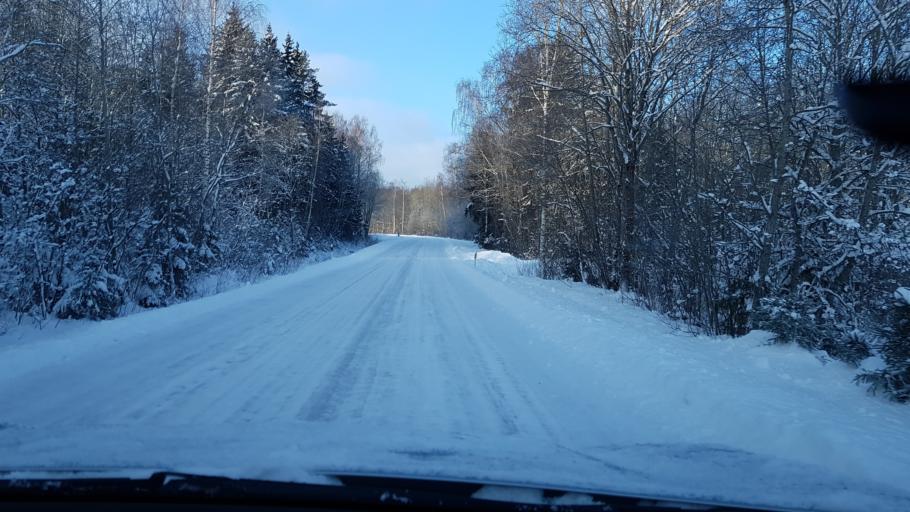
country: EE
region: Harju
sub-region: Nissi vald
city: Turba
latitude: 59.1038
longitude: 24.2432
